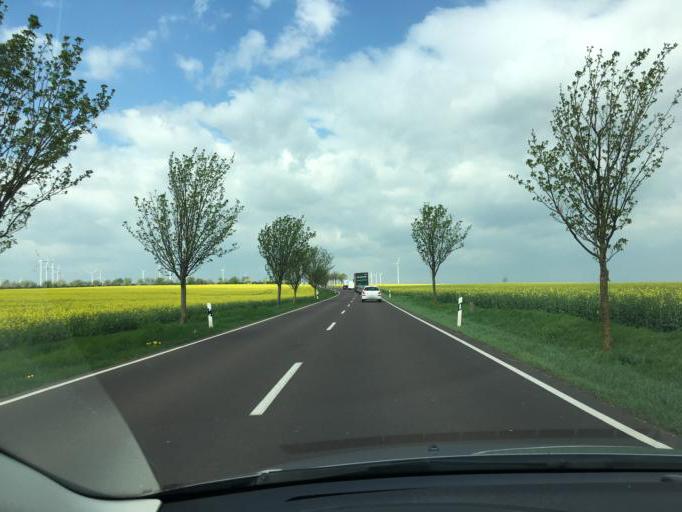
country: DE
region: Saxony-Anhalt
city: Sandersleben
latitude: 51.7195
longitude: 11.6026
